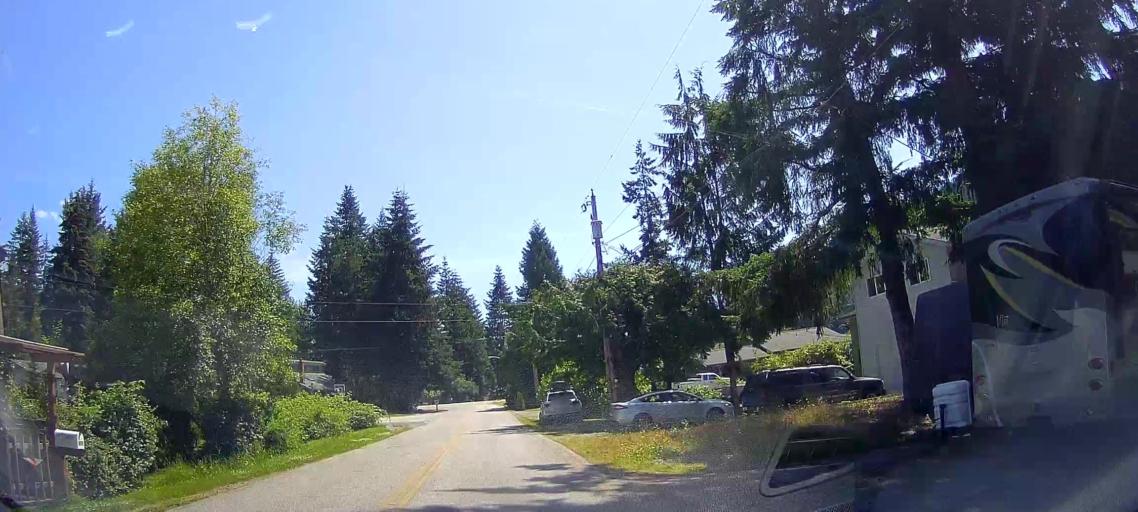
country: US
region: Washington
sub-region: Whatcom County
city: Sudden Valley
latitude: 48.6543
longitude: -122.3302
